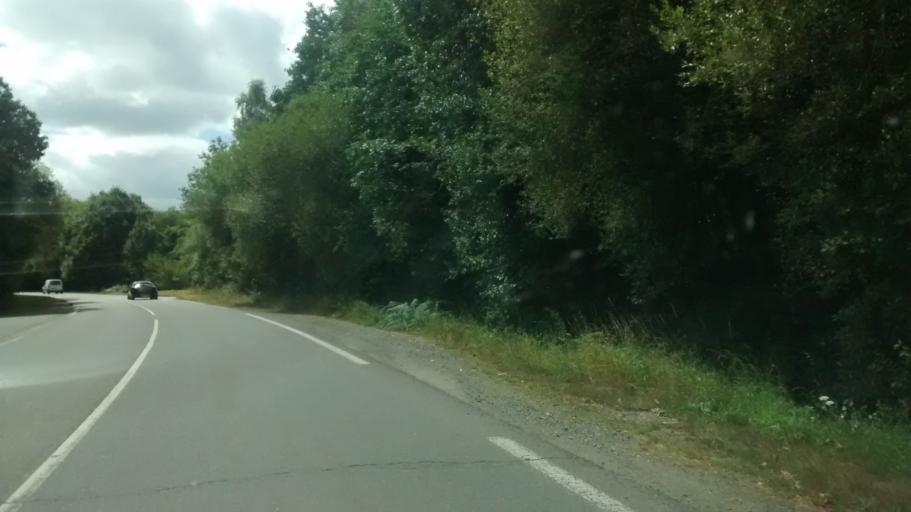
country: FR
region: Brittany
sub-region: Departement d'Ille-et-Vilaine
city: Hede-Bazouges
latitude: 48.2969
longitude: -1.8221
